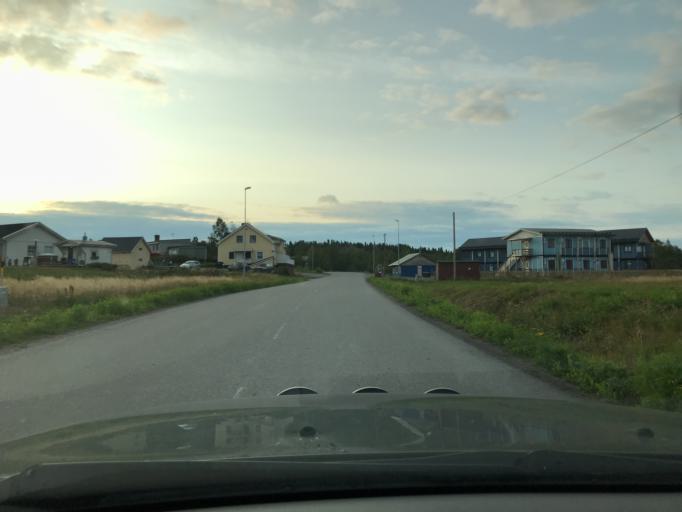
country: SE
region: Norrbotten
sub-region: Gallivare Kommun
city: Malmberget
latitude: 67.6457
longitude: 21.0517
